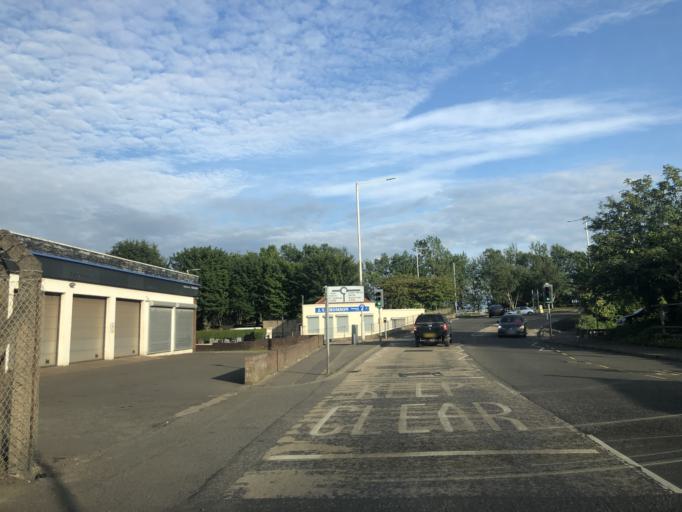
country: GB
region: Scotland
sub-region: Fife
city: Leven
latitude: 56.1938
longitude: -3.0021
